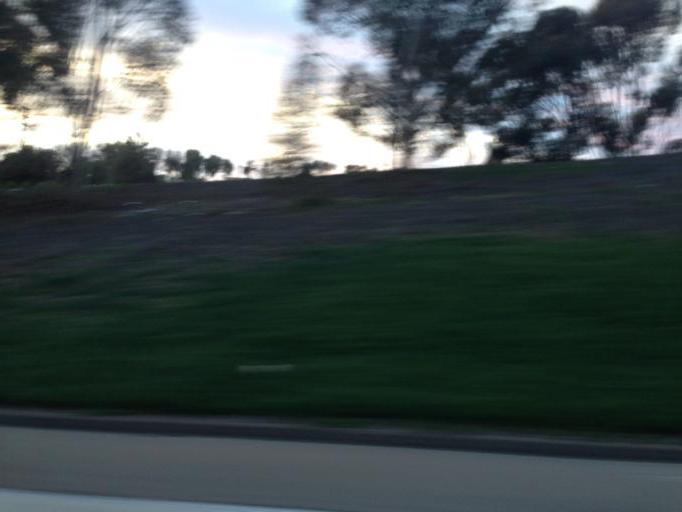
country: US
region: California
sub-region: San Diego County
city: San Diego
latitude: 32.7368
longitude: -117.1144
